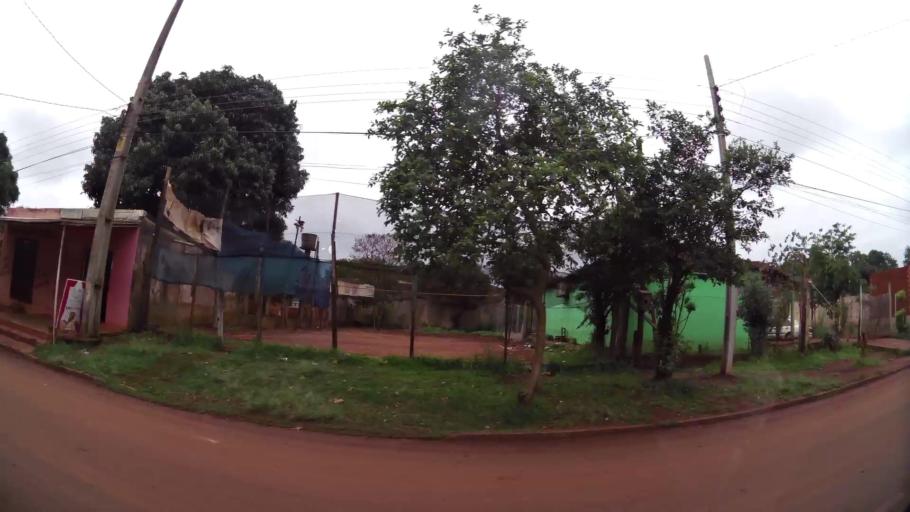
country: PY
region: Alto Parana
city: Presidente Franco
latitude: -25.5083
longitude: -54.6884
